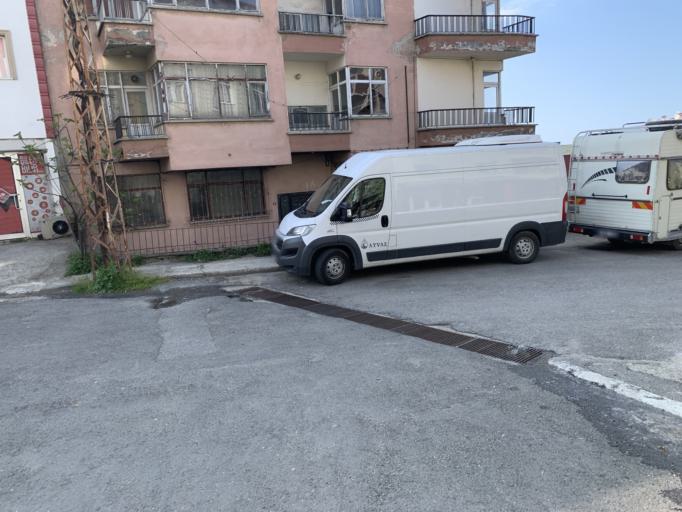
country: TR
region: Trabzon
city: Trabzon
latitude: 40.9964
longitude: 39.7603
